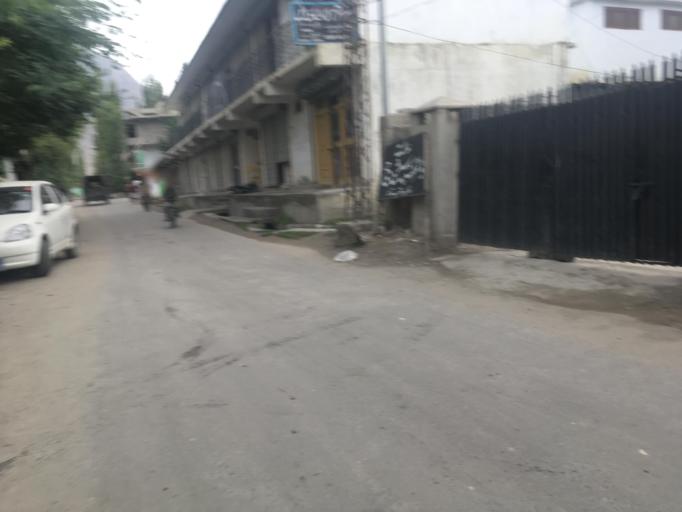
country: PK
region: Gilgit-Baltistan
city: Skardu
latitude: 35.2933
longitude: 75.6490
